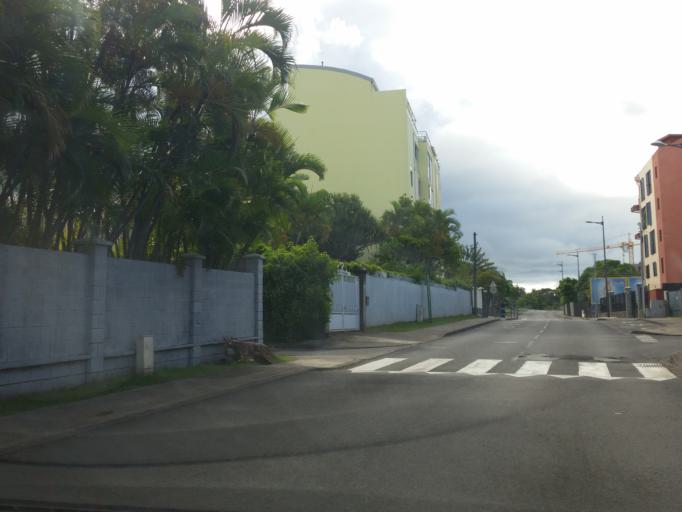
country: RE
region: Reunion
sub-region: Reunion
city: Saint-Denis
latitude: -20.8982
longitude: 55.4785
